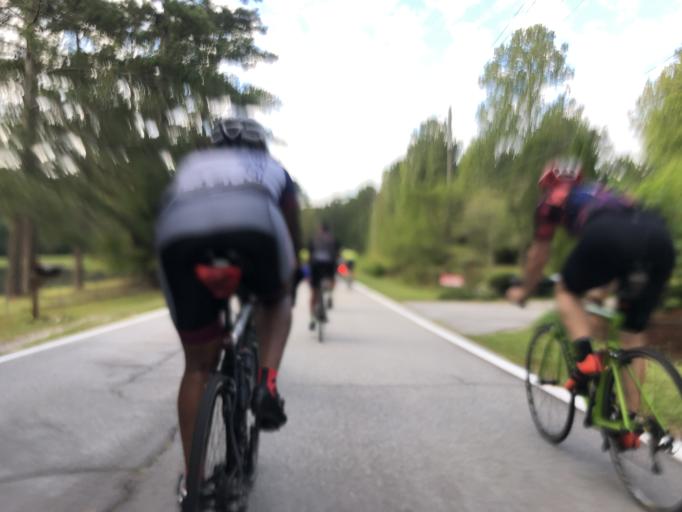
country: US
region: Georgia
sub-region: Fulton County
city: Fairburn
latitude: 33.5983
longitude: -84.6535
